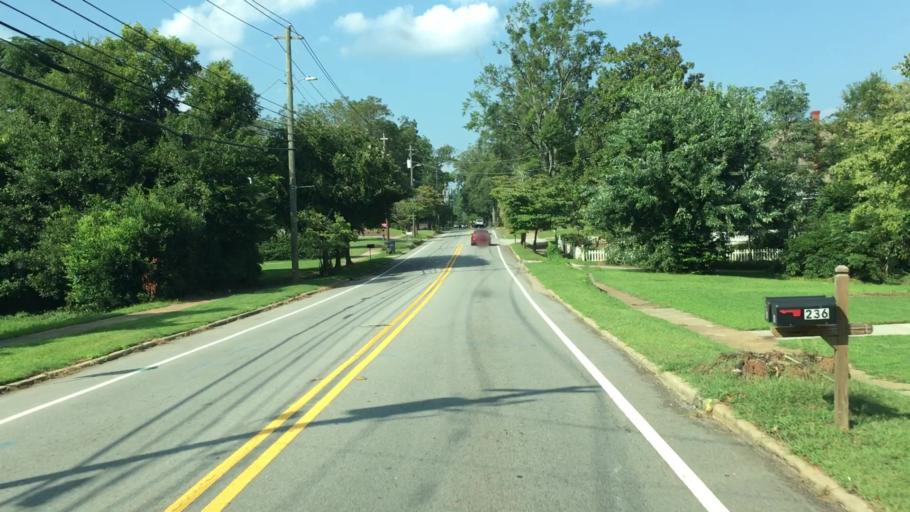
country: US
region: Georgia
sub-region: Walton County
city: Social Circle
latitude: 33.6582
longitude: -83.7172
